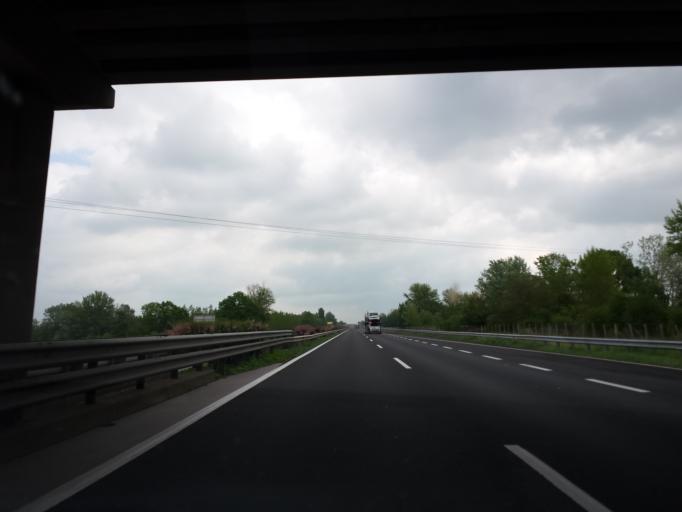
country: HU
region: Gyor-Moson-Sopron
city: Kimle
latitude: 47.7877
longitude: 17.3329
